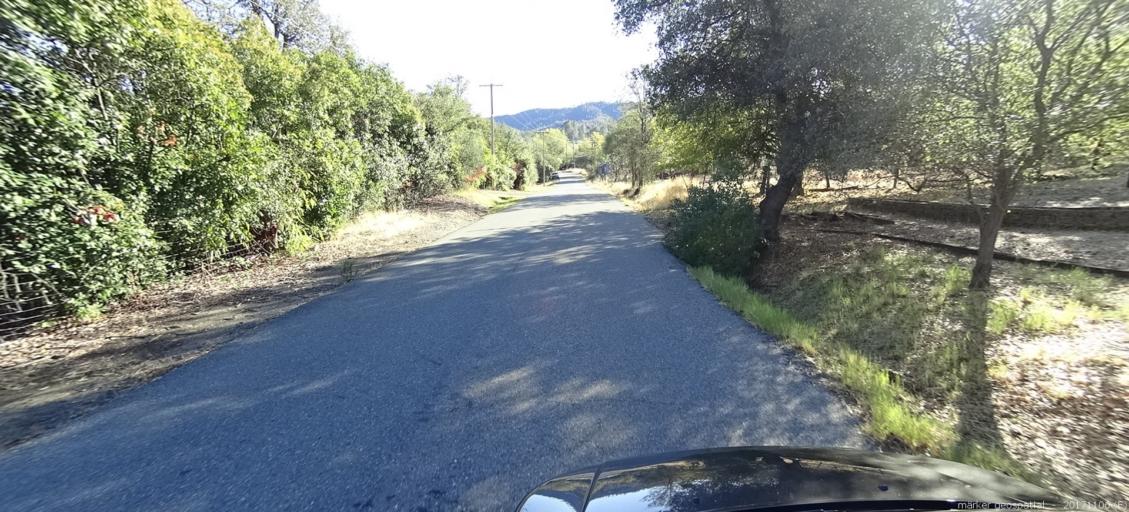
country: US
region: California
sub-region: Shasta County
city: Shasta
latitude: 40.5949
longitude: -122.4884
